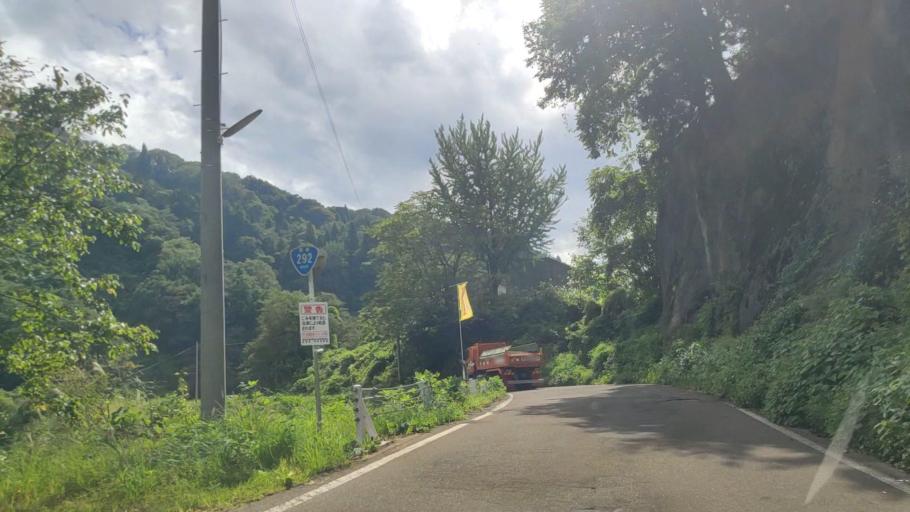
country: JP
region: Niigata
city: Arai
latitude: 36.9454
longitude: 138.2904
